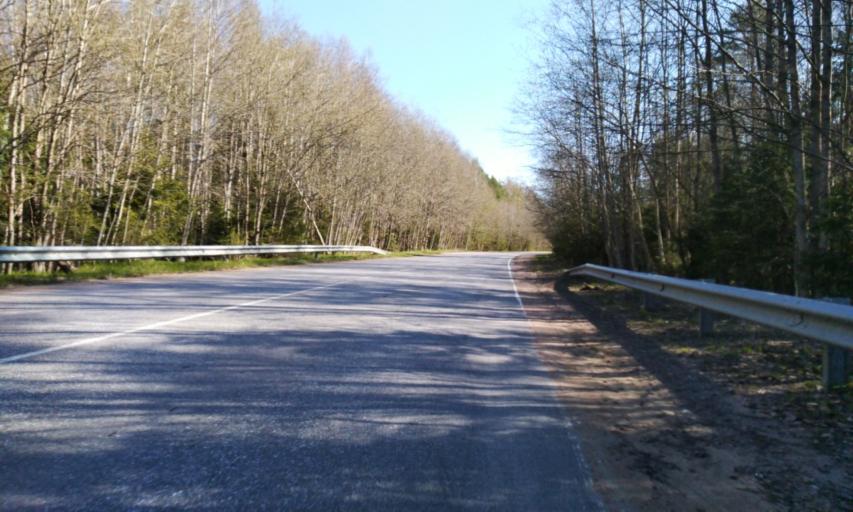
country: RU
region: Leningrad
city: Garbolovo
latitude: 60.3721
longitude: 30.4439
